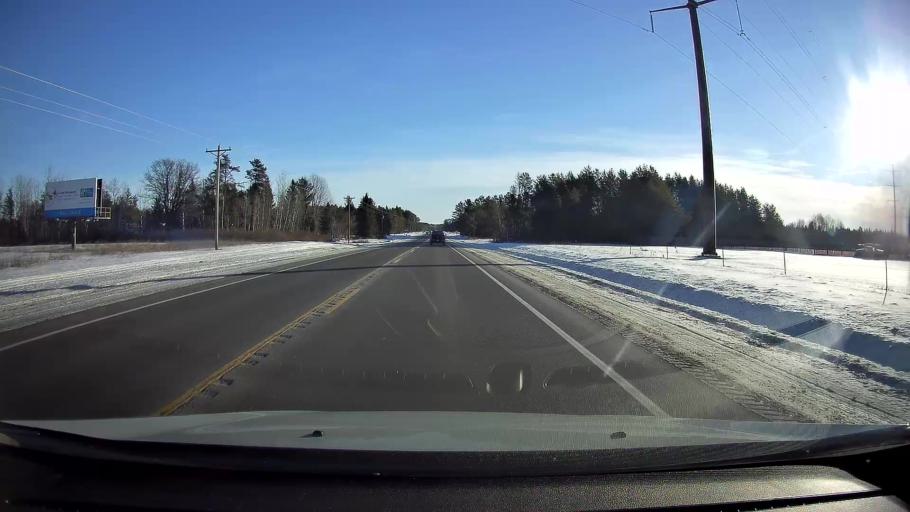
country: US
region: Wisconsin
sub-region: Sawyer County
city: Hayward
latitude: 45.9975
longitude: -91.6121
